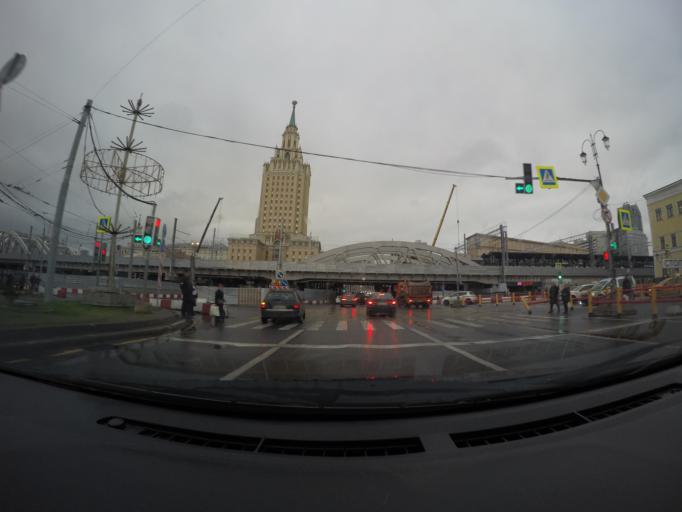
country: RU
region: Moscow
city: Sokol'niki
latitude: 55.7750
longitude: 37.6540
